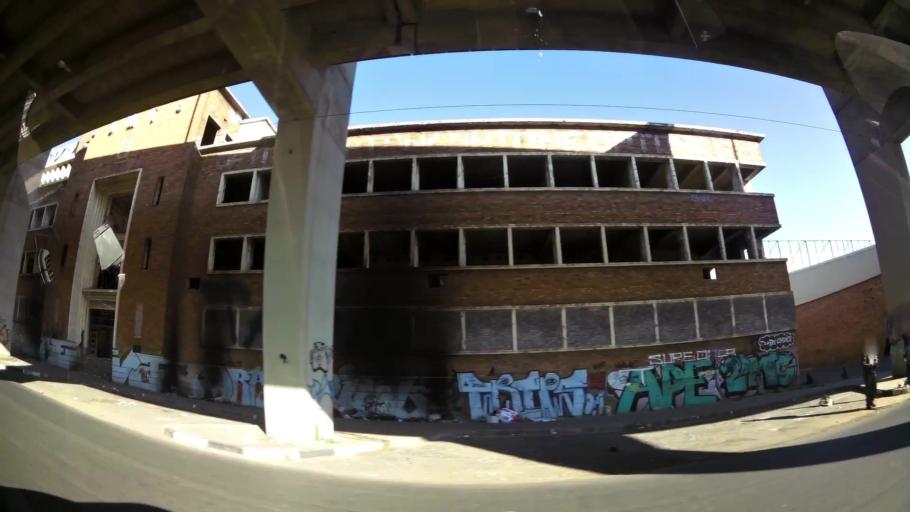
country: ZA
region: Gauteng
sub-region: City of Johannesburg Metropolitan Municipality
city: Johannesburg
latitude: -26.2044
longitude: 28.0304
